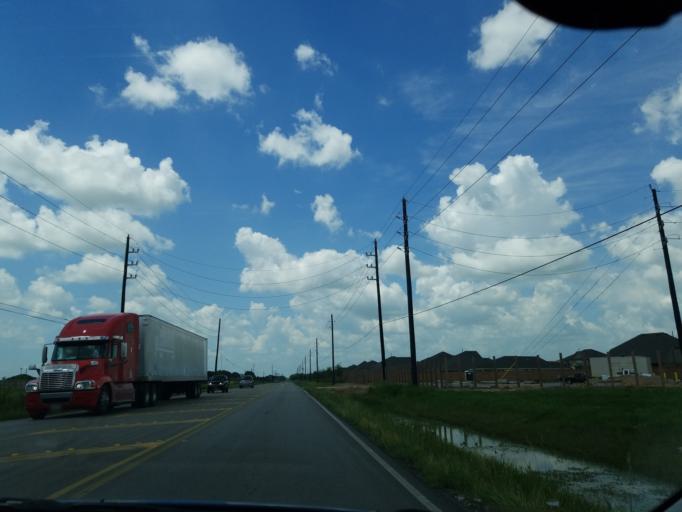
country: US
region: Texas
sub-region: Harris County
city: Katy
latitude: 29.8464
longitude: -95.8069
